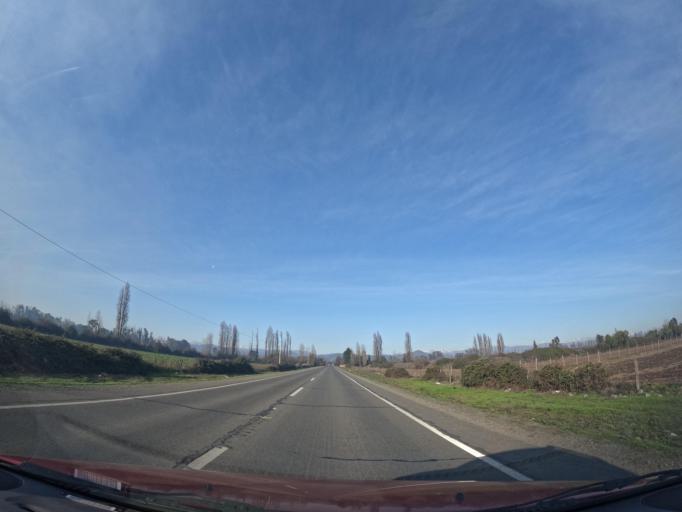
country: CL
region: Maule
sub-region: Provincia de Linares
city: Colbun
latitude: -35.6289
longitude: -71.4463
